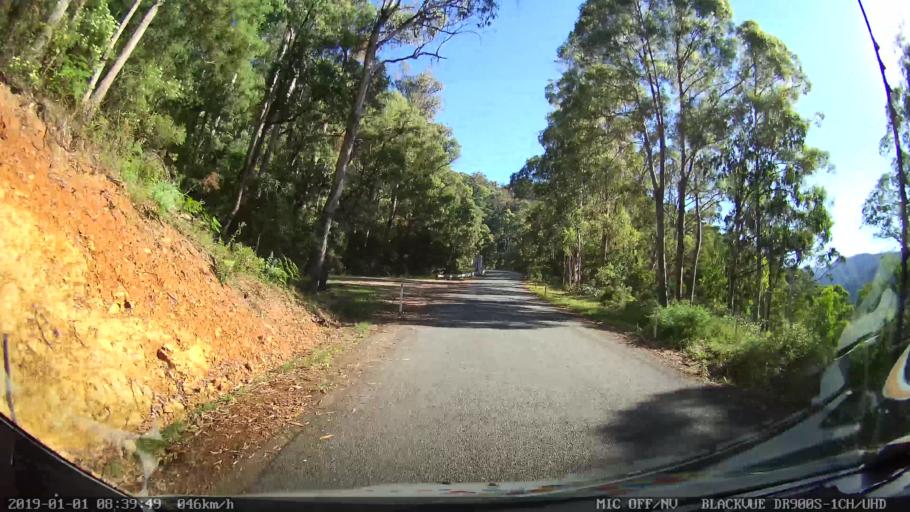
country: AU
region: New South Wales
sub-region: Snowy River
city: Jindabyne
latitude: -36.3288
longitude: 148.1937
